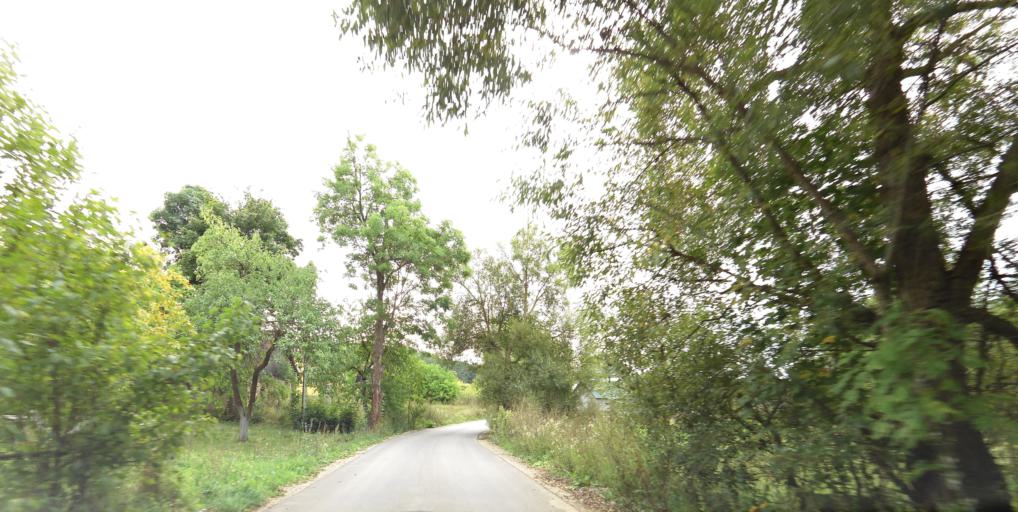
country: LT
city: Grigiskes
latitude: 54.7537
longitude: 25.0281
